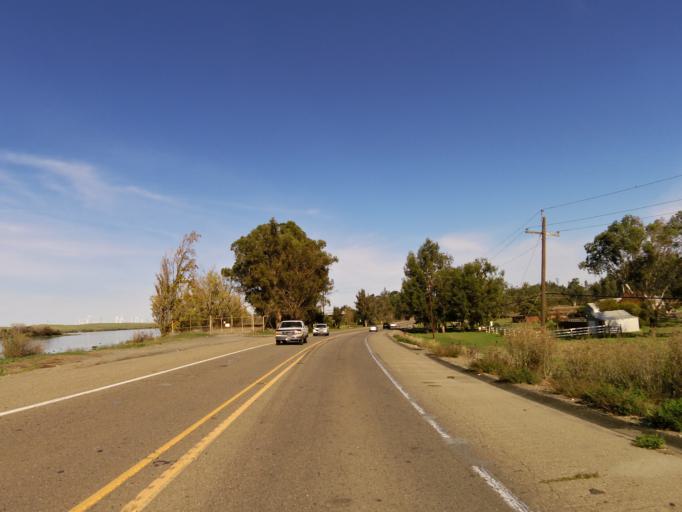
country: US
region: California
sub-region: Solano County
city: Rio Vista
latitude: 38.0975
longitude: -121.7062
